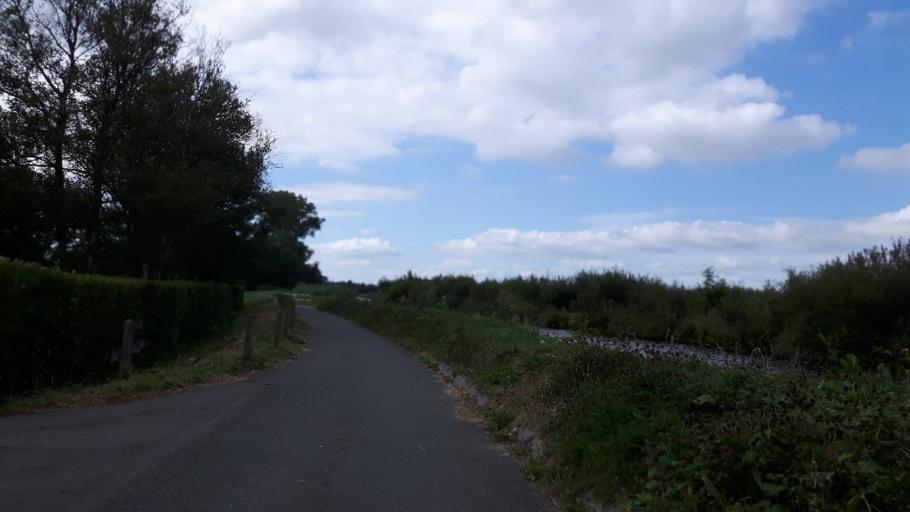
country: NL
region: Utrecht
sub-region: Gemeente De Ronde Venen
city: Mijdrecht
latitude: 52.1526
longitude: 4.8475
